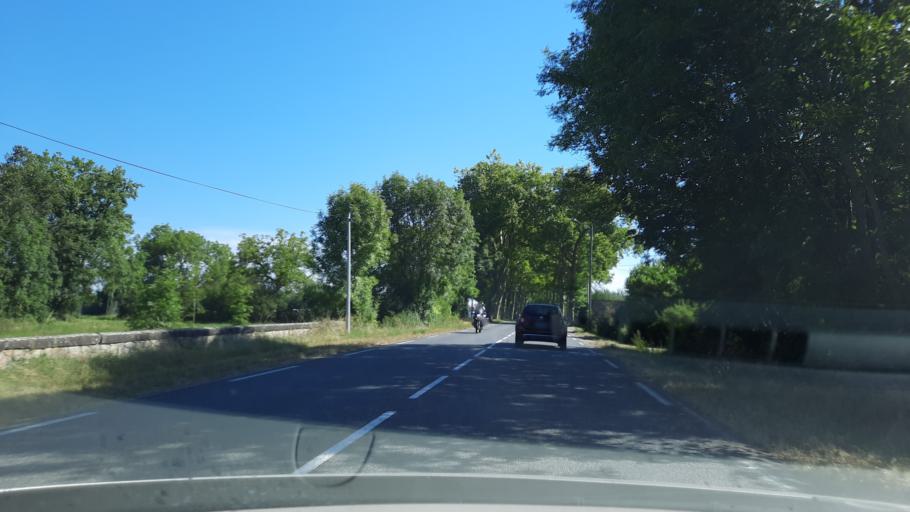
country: FR
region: Midi-Pyrenees
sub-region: Departement du Tarn-et-Garonne
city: Caylus
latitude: 44.3147
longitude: 1.8895
